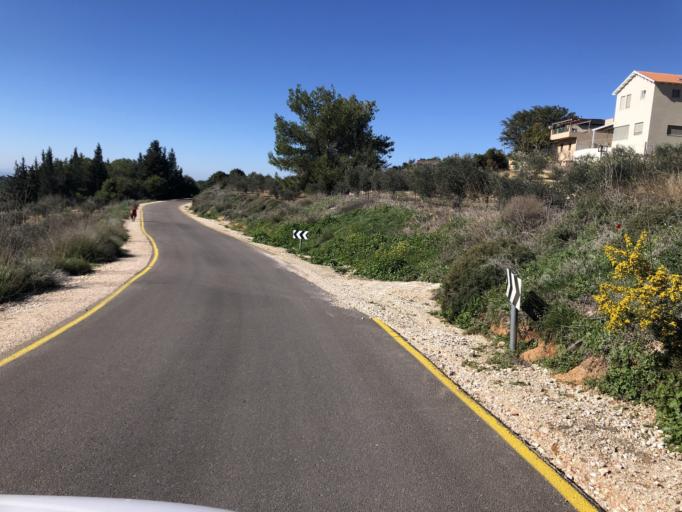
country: IL
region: Jerusalem
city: Zur Hadassa
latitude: 31.7453
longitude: 35.0518
